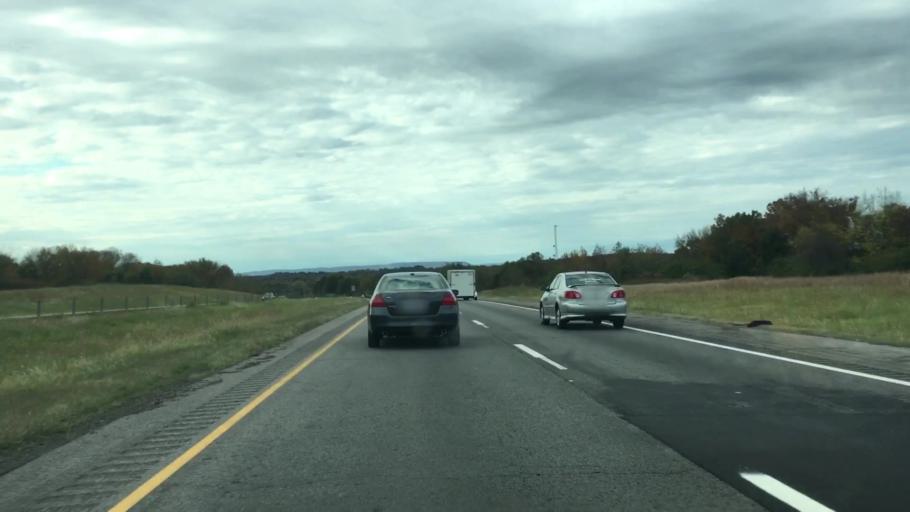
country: US
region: Arkansas
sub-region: Conway County
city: Morrilton
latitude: 35.1716
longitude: -92.6970
